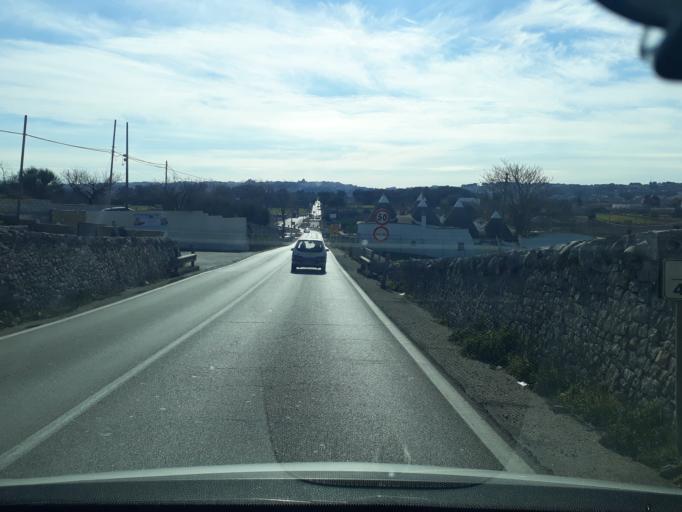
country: IT
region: Apulia
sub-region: Provincia di Bari
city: Locorotondo
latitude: 40.7390
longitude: 17.3325
